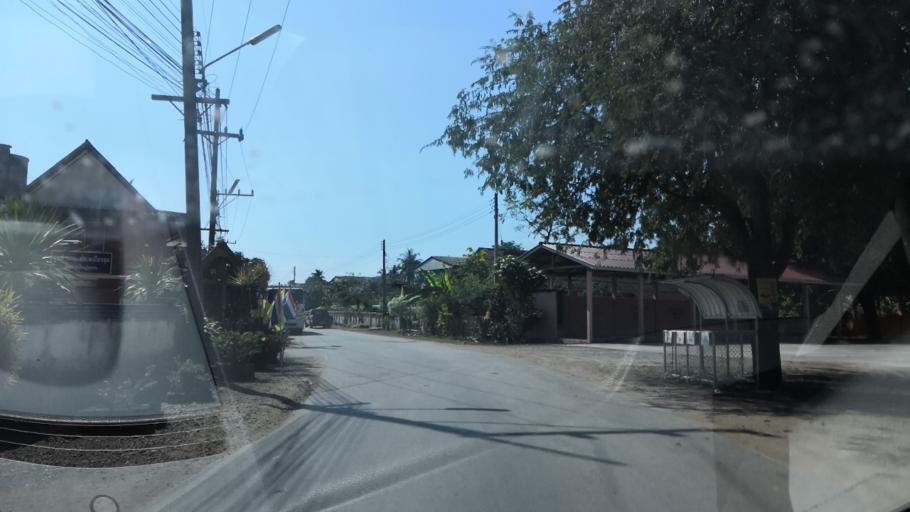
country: TH
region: Chiang Rai
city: Wiang Chai
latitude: 19.8919
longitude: 99.9516
